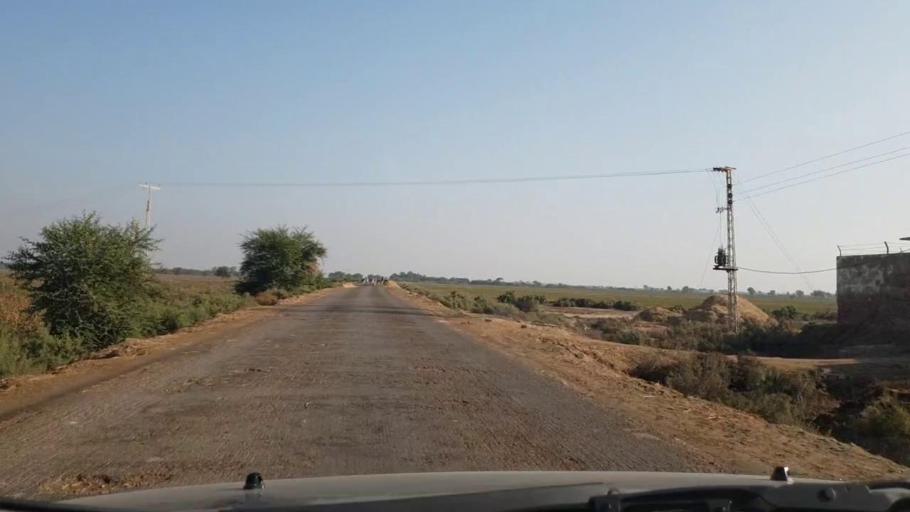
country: PK
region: Sindh
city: Tando Bago
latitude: 24.8560
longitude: 69.0419
